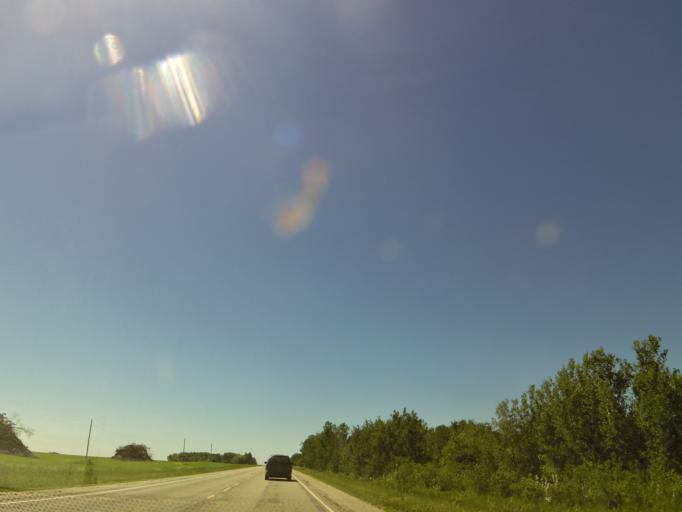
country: US
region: Minnesota
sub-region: Mahnomen County
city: Mahnomen
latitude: 47.4192
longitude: -95.9747
